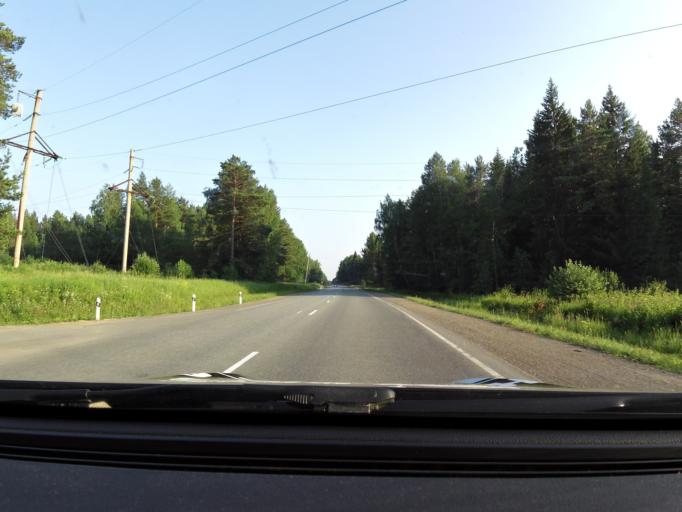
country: RU
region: Sverdlovsk
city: Nizhniye Sergi
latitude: 56.6080
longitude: 59.2286
